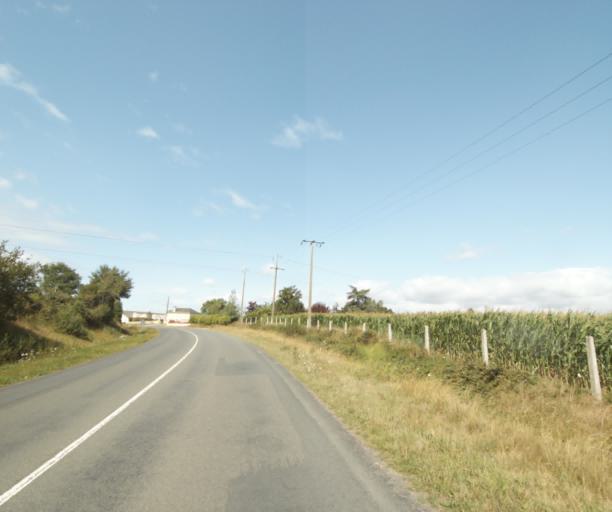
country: FR
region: Pays de la Loire
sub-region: Departement de la Sarthe
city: Sable-sur-Sarthe
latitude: 47.8409
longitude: -0.3550
